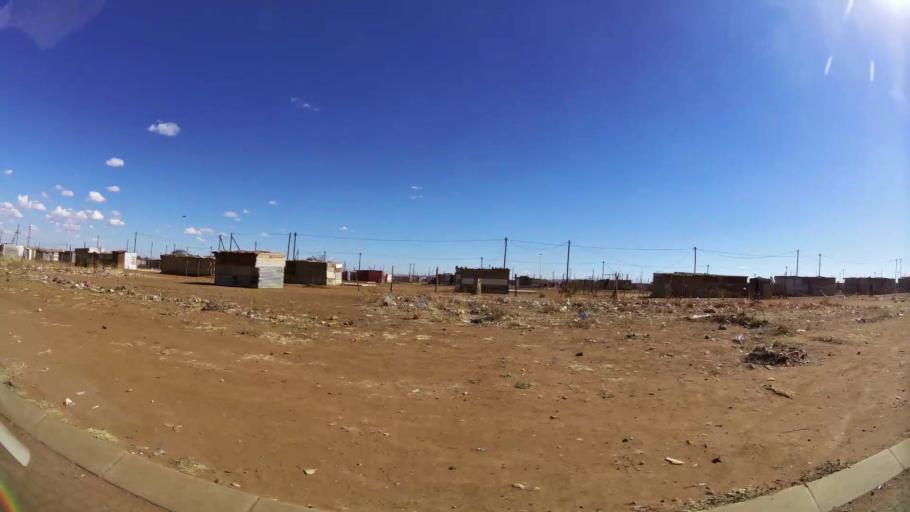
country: ZA
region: North-West
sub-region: Dr Kenneth Kaunda District Municipality
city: Klerksdorp
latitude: -26.8700
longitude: 26.5649
